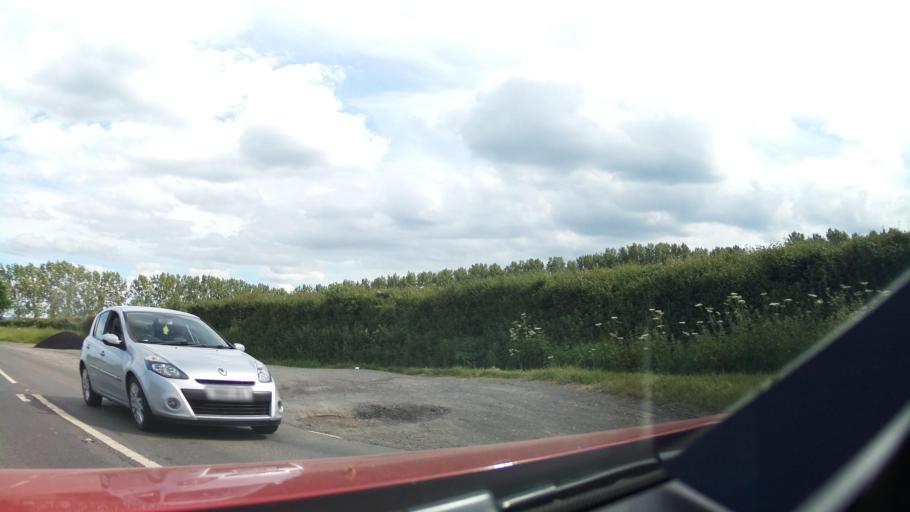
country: GB
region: England
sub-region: Worcestershire
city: Pershore
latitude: 52.1039
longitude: -2.0433
